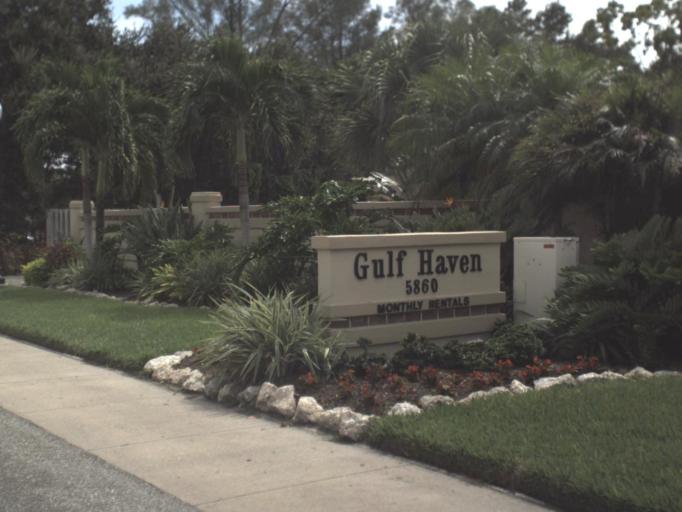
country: US
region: Florida
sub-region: Sarasota County
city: South Sarasota
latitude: 27.2643
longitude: -82.5425
